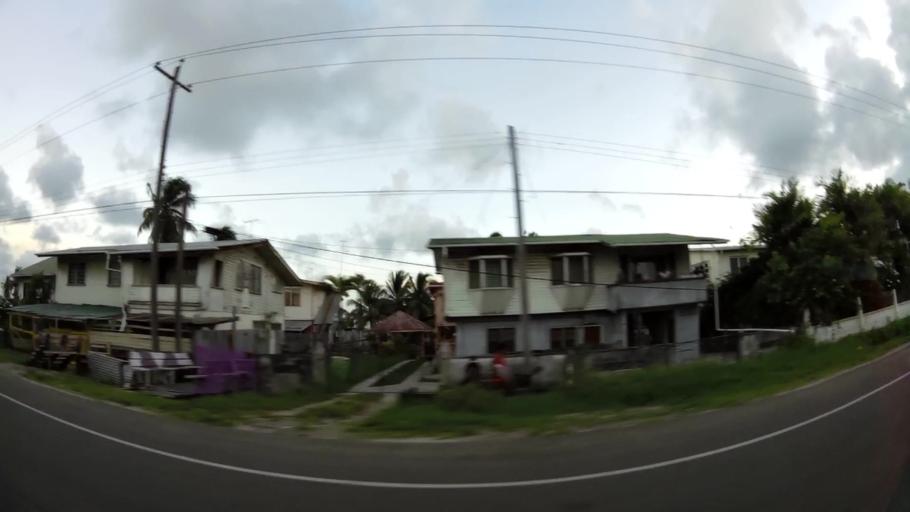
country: GY
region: Demerara-Mahaica
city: Georgetown
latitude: 6.8214
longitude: -58.0980
